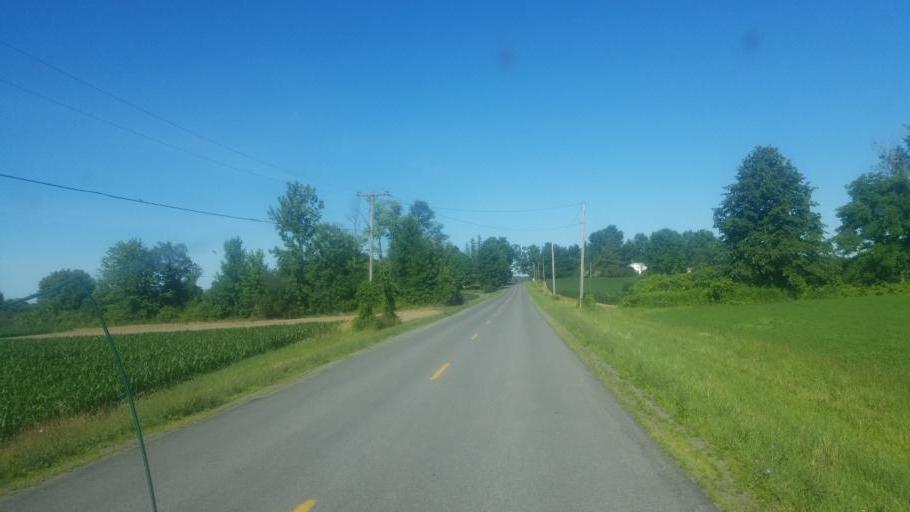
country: US
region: New York
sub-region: Ontario County
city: Clifton Springs
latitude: 42.8390
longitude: -77.1298
